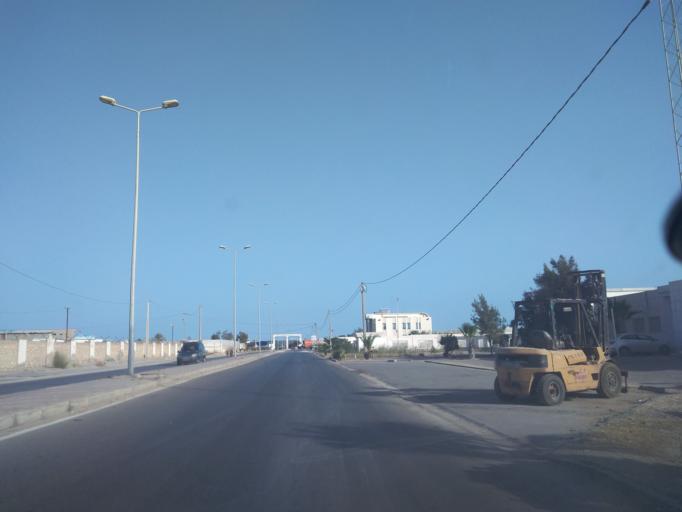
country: TN
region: Safaqis
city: Sfax
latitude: 34.7238
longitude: 10.7580
